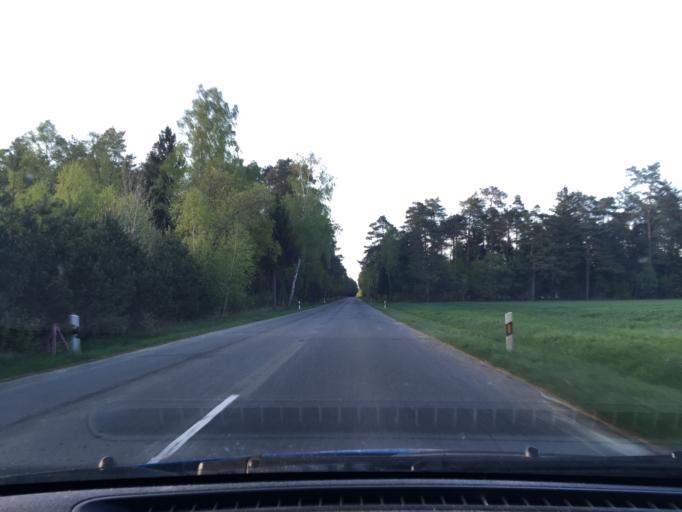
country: DE
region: Lower Saxony
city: Wietzendorf
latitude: 52.9728
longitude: 9.9812
